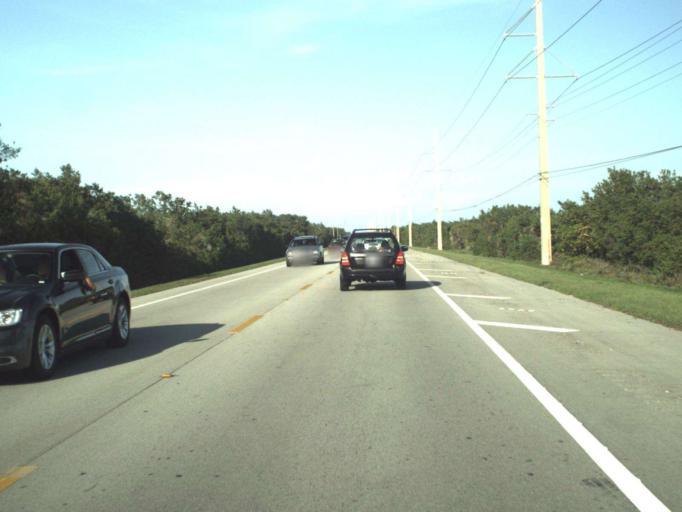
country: US
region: Florida
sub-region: Monroe County
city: Marathon
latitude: 24.7848
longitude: -80.9018
